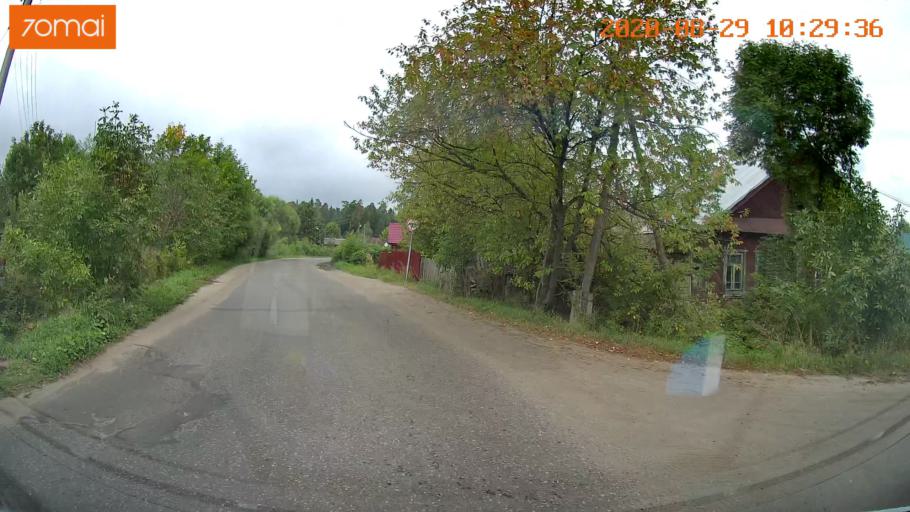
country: RU
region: Ivanovo
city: Yur'yevets
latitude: 57.3115
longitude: 43.0970
